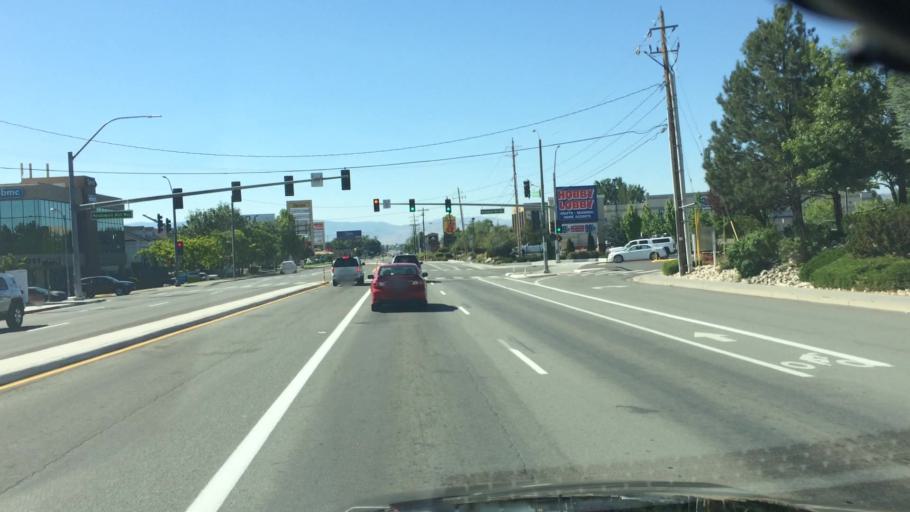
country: US
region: Nevada
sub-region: Washoe County
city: Reno
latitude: 39.4748
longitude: -119.7882
